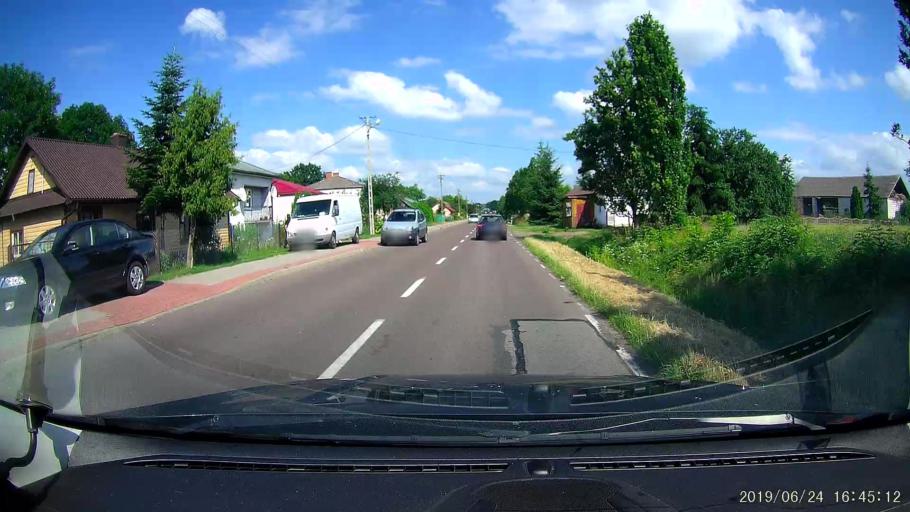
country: PL
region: Lublin Voivodeship
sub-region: Powiat tomaszowski
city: Laszczow
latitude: 50.5327
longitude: 23.6646
